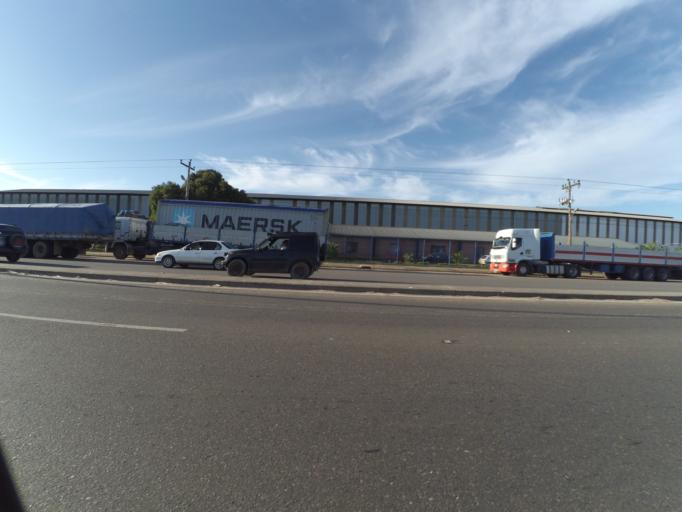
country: BO
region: Santa Cruz
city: Santa Cruz de la Sierra
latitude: -17.7741
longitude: -63.1322
